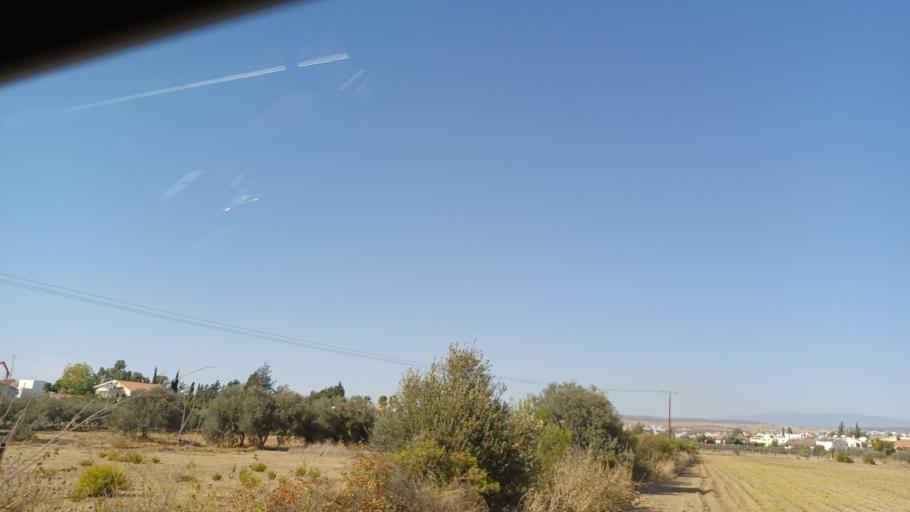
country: CY
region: Larnaka
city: Kolossi
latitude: 34.6657
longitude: 32.9380
